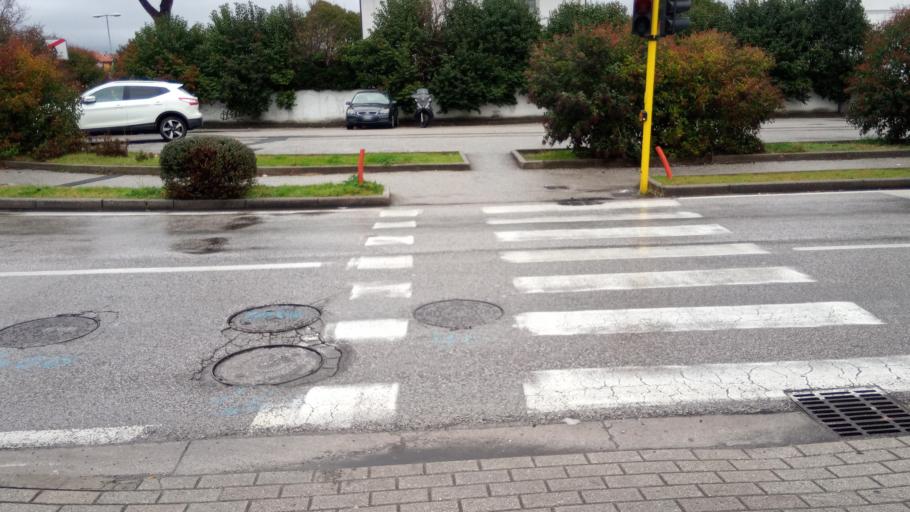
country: IT
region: Tuscany
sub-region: Province of Pisa
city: Pisa
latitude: 43.7205
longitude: 10.4219
